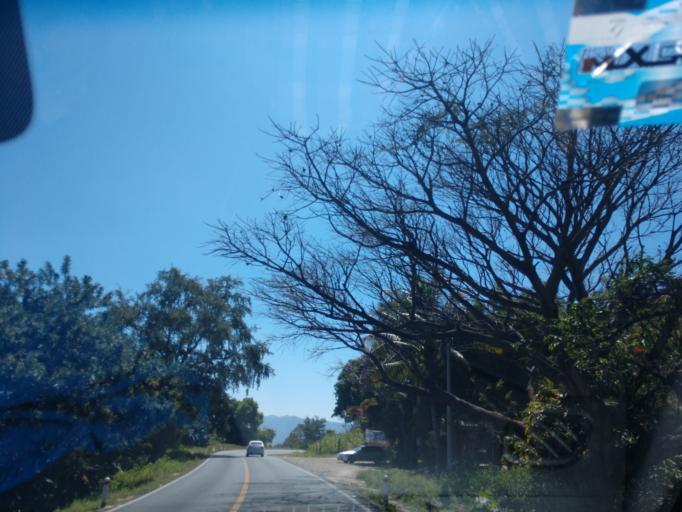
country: MX
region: Nayarit
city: Xalisco
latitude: 21.4083
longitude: -104.8967
